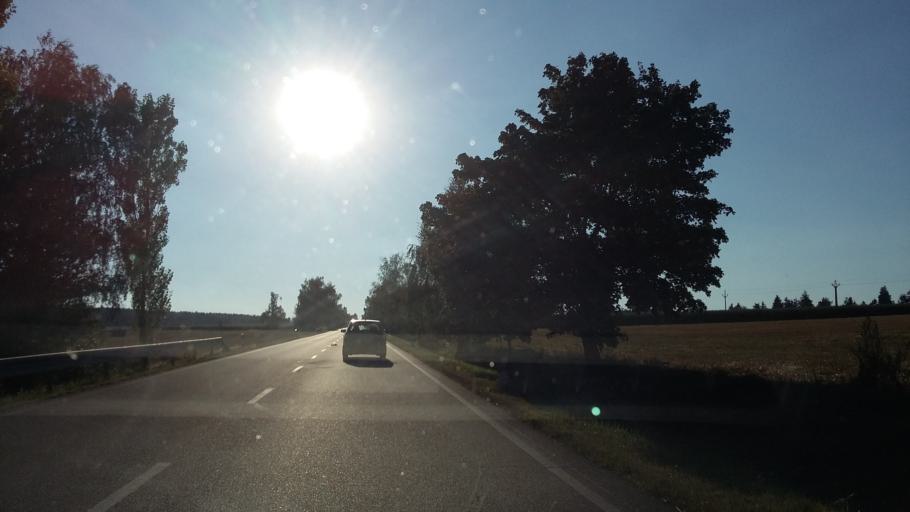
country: CZ
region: Vysocina
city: Merin
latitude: 49.4006
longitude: 15.8416
